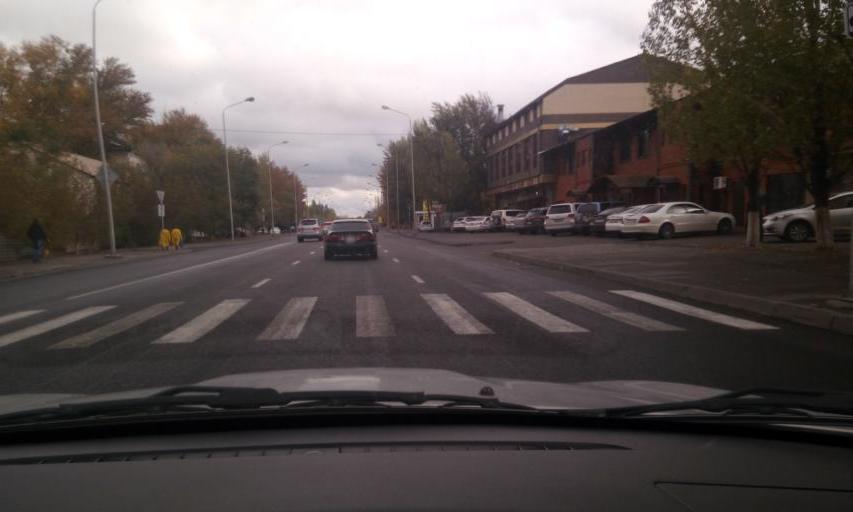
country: KZ
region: Astana Qalasy
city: Astana
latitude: 51.1691
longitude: 71.4537
